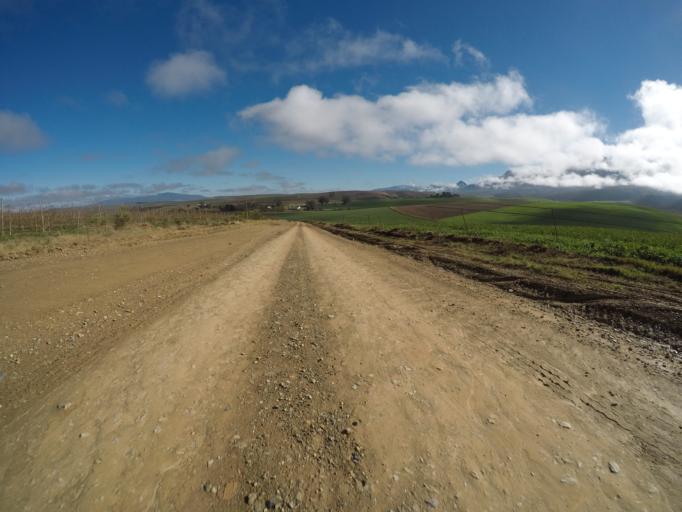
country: ZA
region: Western Cape
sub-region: Overberg District Municipality
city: Caledon
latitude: -34.1093
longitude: 19.7589
